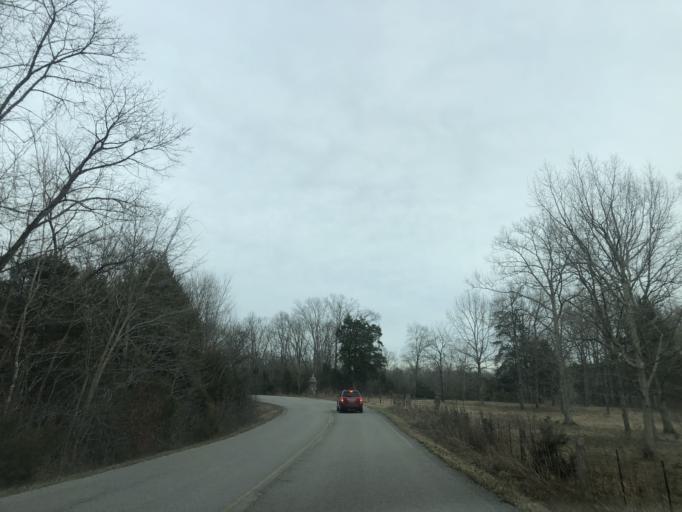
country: US
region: Tennessee
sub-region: Wilson County
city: Lebanon
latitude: 36.2557
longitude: -86.2744
